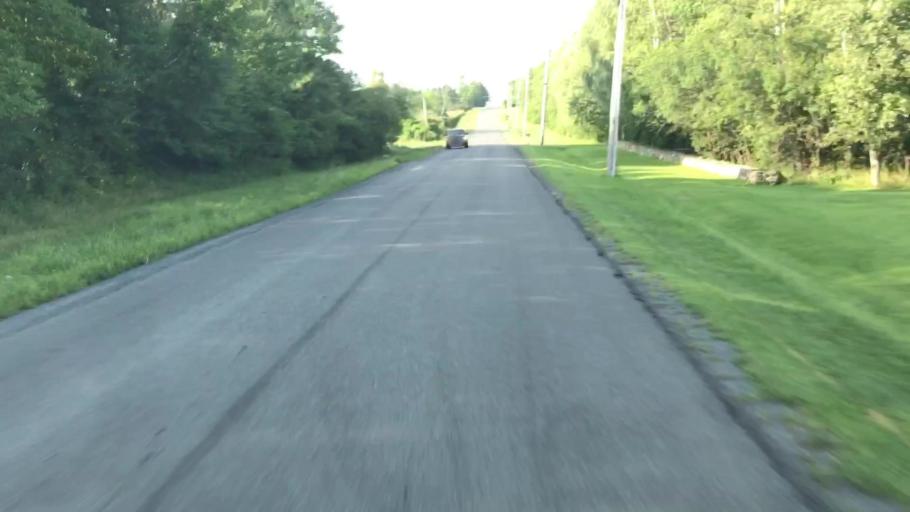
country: US
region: New York
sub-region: Onondaga County
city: Skaneateles
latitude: 42.9472
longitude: -76.4587
